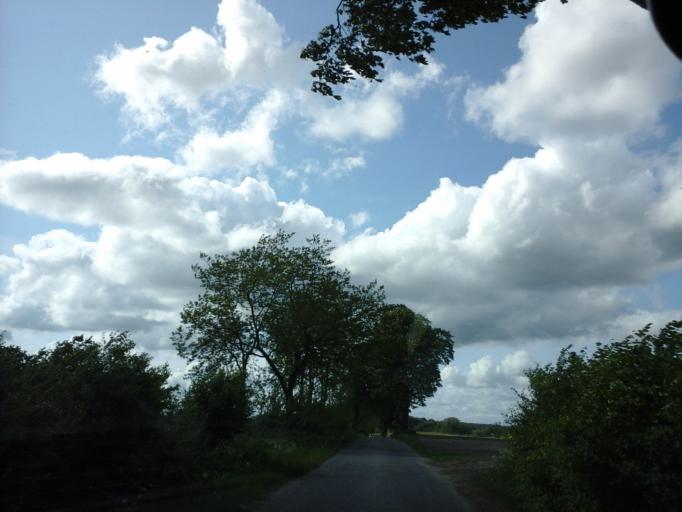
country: PL
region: West Pomeranian Voivodeship
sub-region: Powiat choszczenski
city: Choszczno
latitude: 53.1353
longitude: 15.3633
